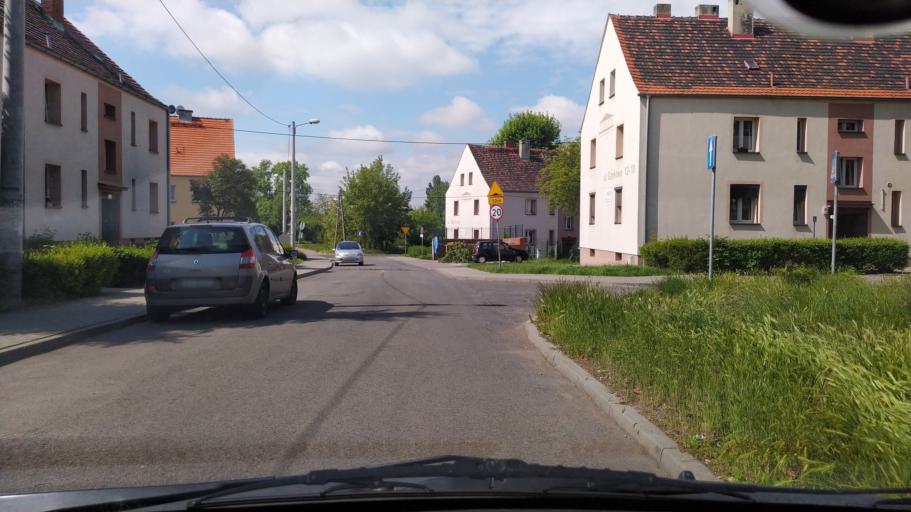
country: PL
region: Silesian Voivodeship
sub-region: Gliwice
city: Gliwice
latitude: 50.2901
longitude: 18.7218
